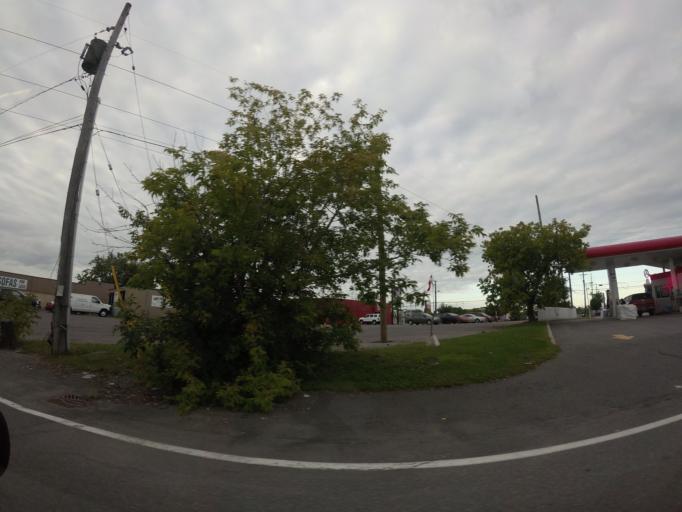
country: CA
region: Ontario
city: Ottawa
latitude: 45.4252
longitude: -75.6368
